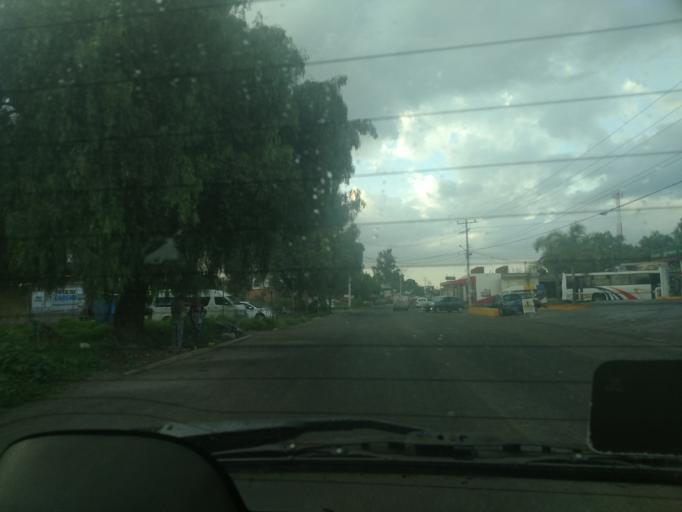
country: MX
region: Morelos
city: Coyotepec
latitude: 19.7687
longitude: -99.2015
